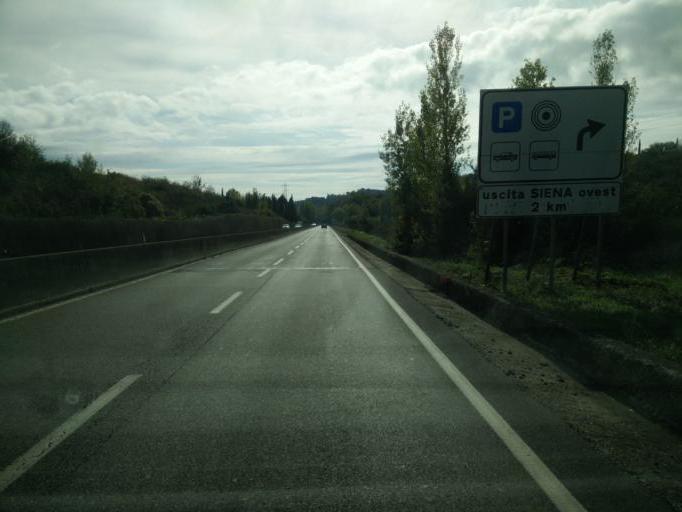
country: IT
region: Tuscany
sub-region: Provincia di Siena
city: Belverde
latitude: 43.3242
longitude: 11.2975
